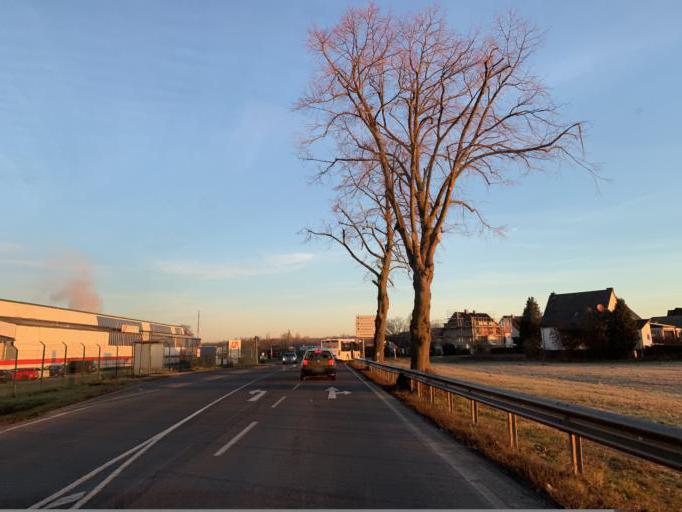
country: DE
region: North Rhine-Westphalia
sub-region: Regierungsbezirk Koln
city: Inden
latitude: 50.8959
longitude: 6.3897
